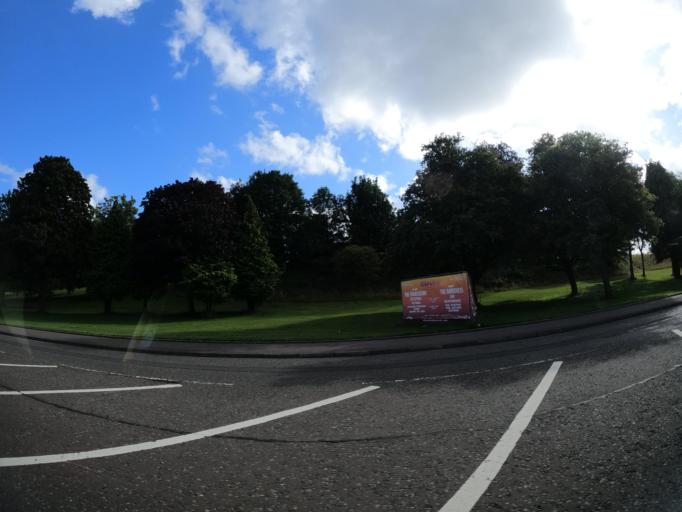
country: GB
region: Scotland
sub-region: Falkirk
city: Falkirk
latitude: 55.9969
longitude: -3.7620
